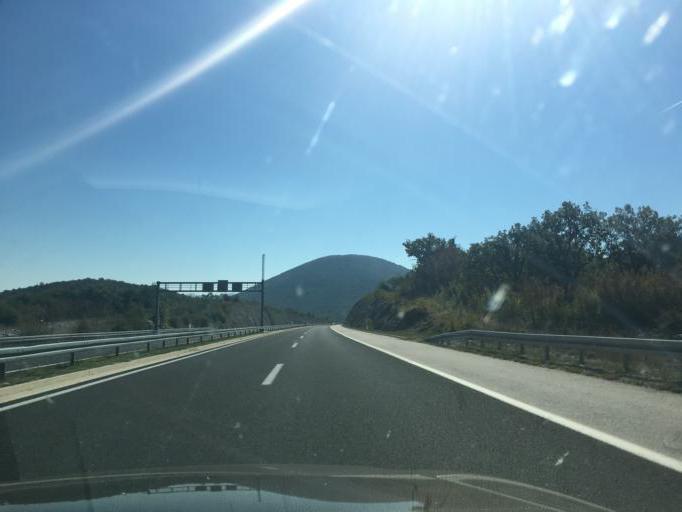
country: HR
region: Splitsko-Dalmatinska
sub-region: Grad Trogir
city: Trogir
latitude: 43.6431
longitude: 16.2043
